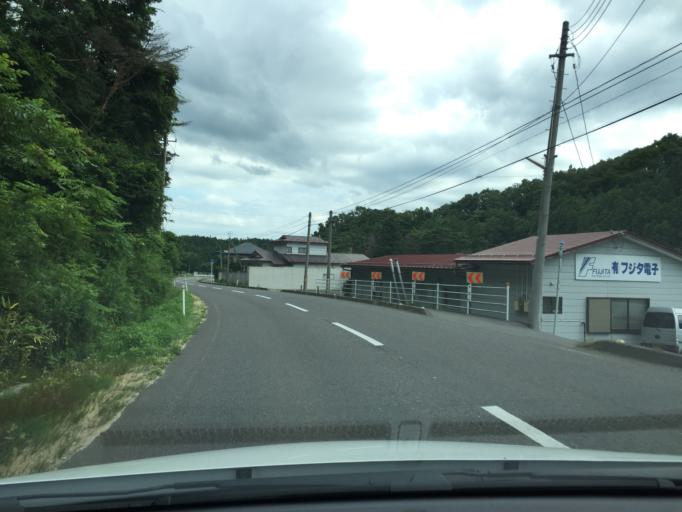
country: JP
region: Fukushima
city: Sukagawa
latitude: 37.3046
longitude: 140.2091
